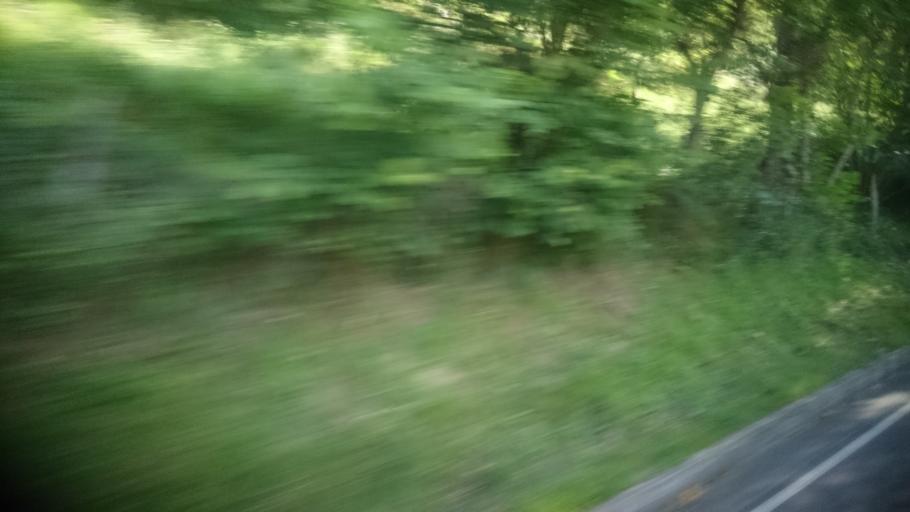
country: ES
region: Asturias
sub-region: Province of Asturias
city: Amieva
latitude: 43.3017
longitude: -5.0375
